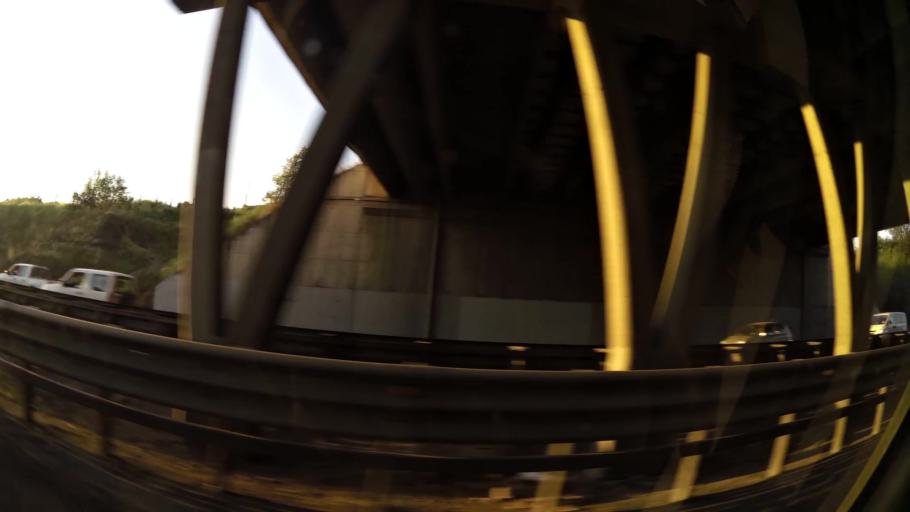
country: CL
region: Santiago Metropolitan
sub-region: Provincia de Santiago
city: Lo Prado
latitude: -33.4839
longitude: -70.7247
